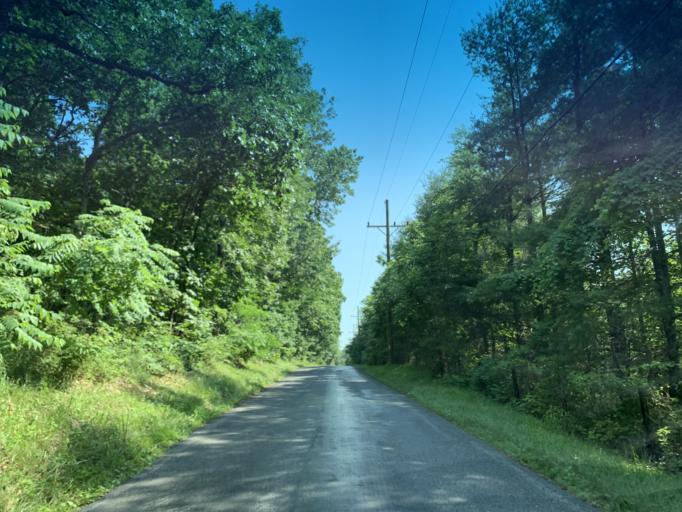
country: US
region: Maryland
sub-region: Montgomery County
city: Poolesville
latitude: 39.1544
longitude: -77.4533
